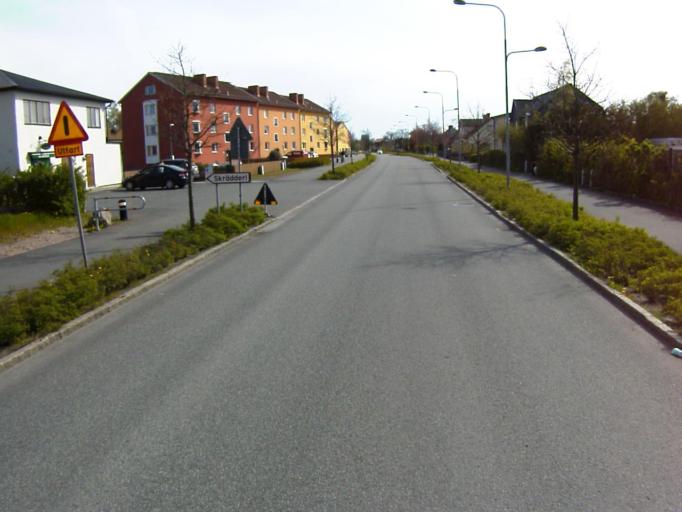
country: SE
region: Skane
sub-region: Kristianstads Kommun
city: Kristianstad
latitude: 56.0491
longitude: 14.1547
